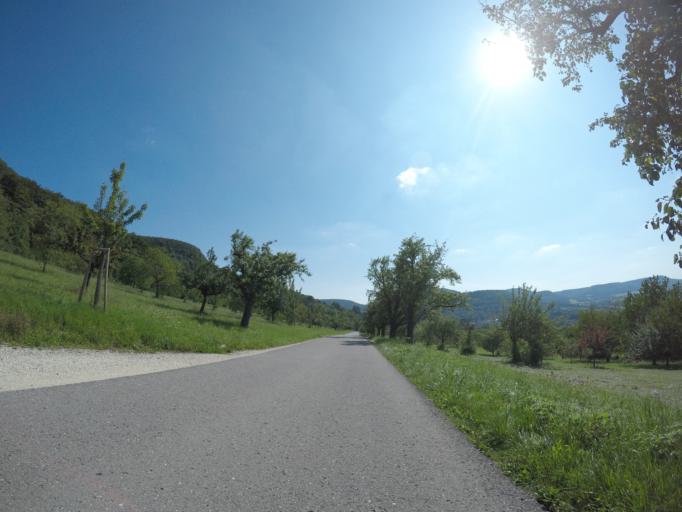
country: DE
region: Baden-Wuerttemberg
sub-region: Tuebingen Region
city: Pfullingen
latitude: 48.4650
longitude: 9.2425
